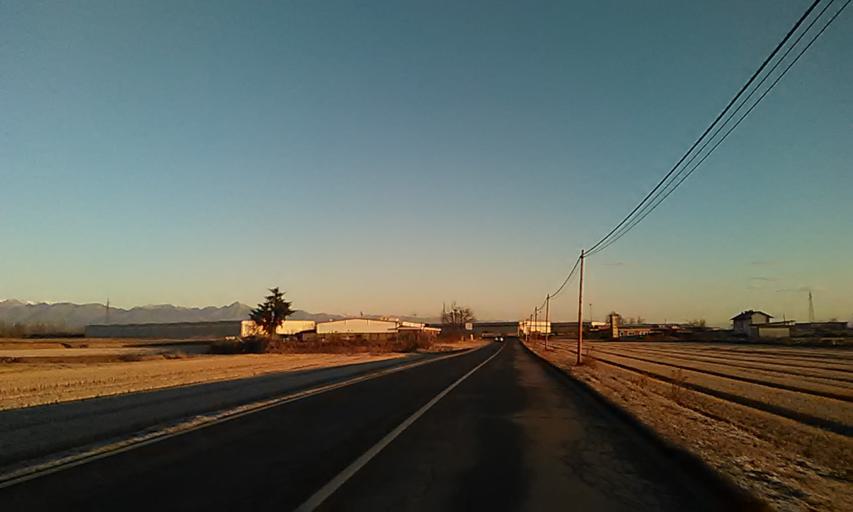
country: IT
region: Piedmont
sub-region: Provincia di Vercelli
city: Carisio
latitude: 45.4239
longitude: 8.2118
